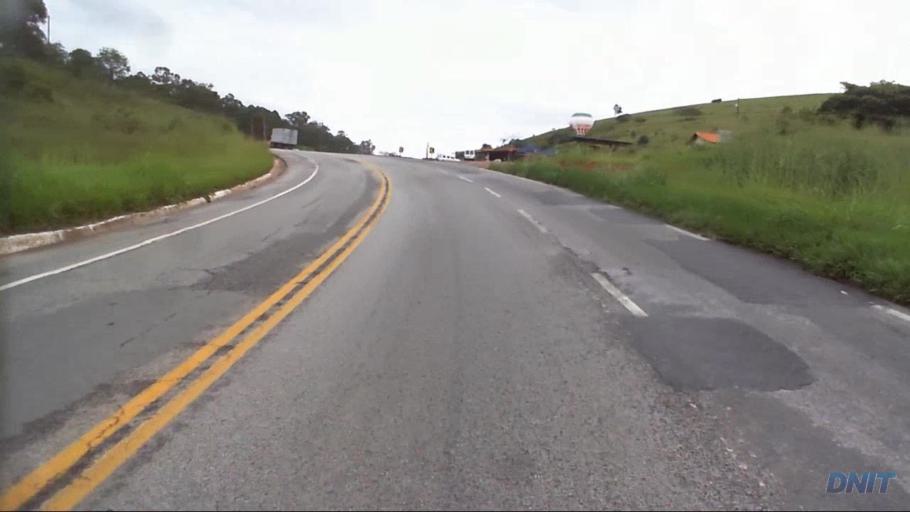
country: BR
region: Minas Gerais
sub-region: Joao Monlevade
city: Joao Monlevade
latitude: -19.8497
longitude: -43.2812
